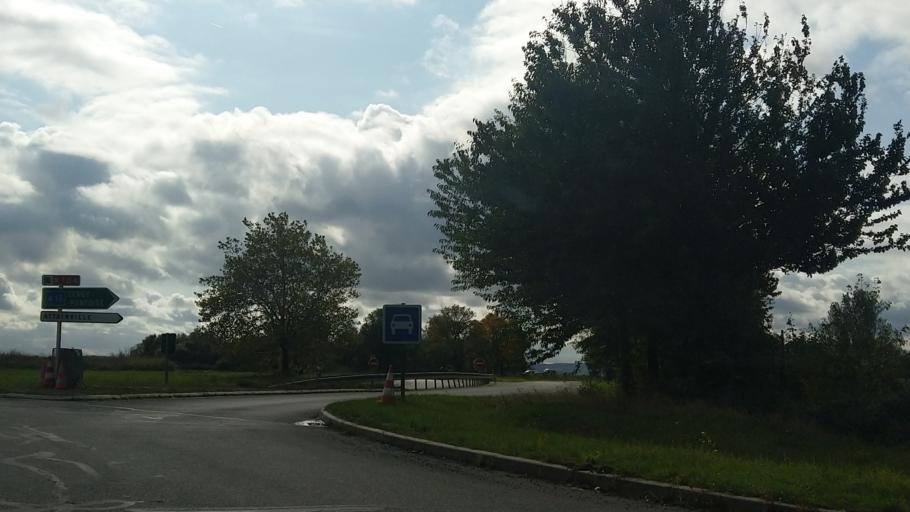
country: FR
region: Ile-de-France
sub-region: Departement du Val-d'Oise
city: Belloy-en-France
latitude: 49.0707
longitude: 2.3854
